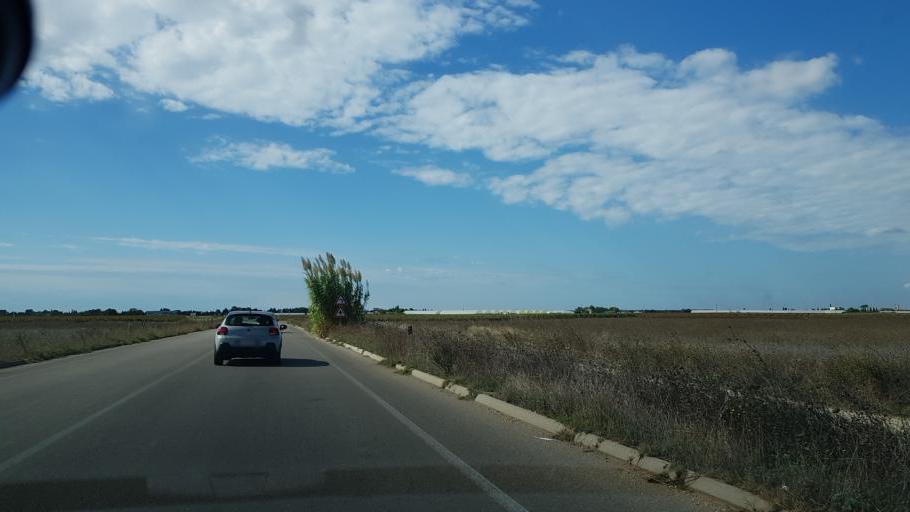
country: IT
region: Apulia
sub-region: Provincia di Lecce
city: Leverano
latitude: 40.3002
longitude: 17.9774
